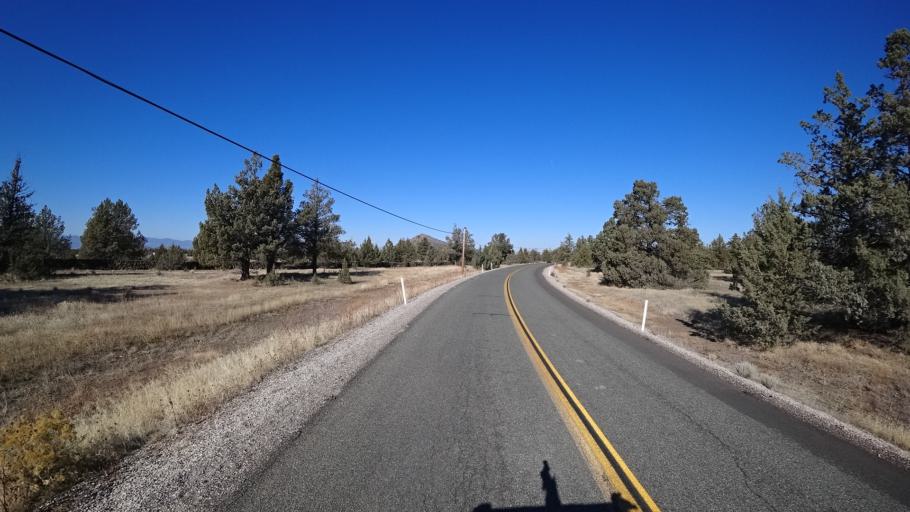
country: US
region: California
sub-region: Siskiyou County
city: Montague
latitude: 41.6471
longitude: -122.3593
